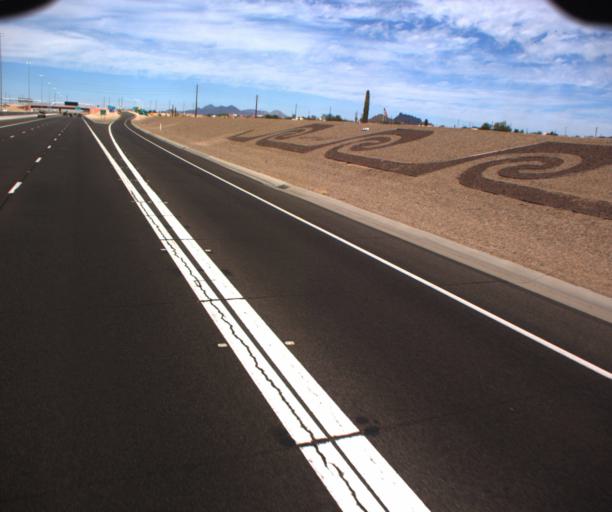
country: US
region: Arizona
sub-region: Pinal County
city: Apache Junction
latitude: 33.4468
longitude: -111.6642
